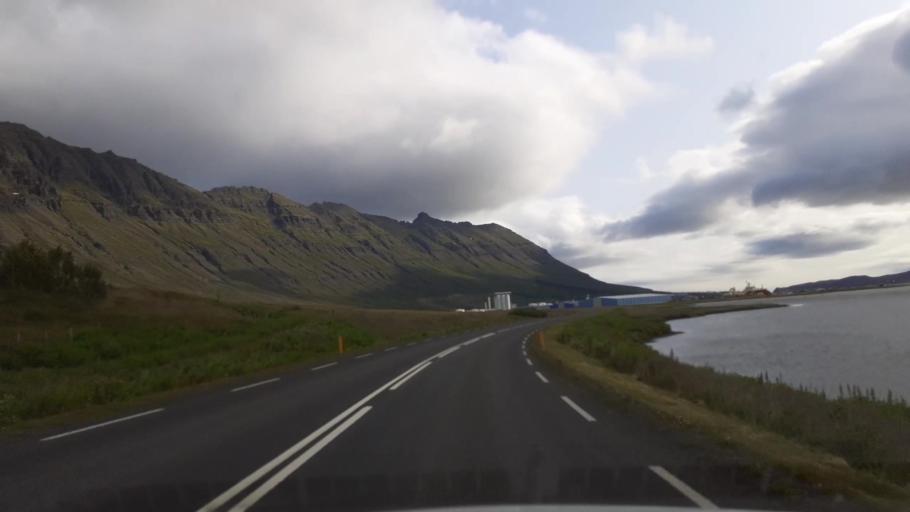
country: IS
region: East
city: Neskaupstadur
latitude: 65.1321
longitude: -13.7599
